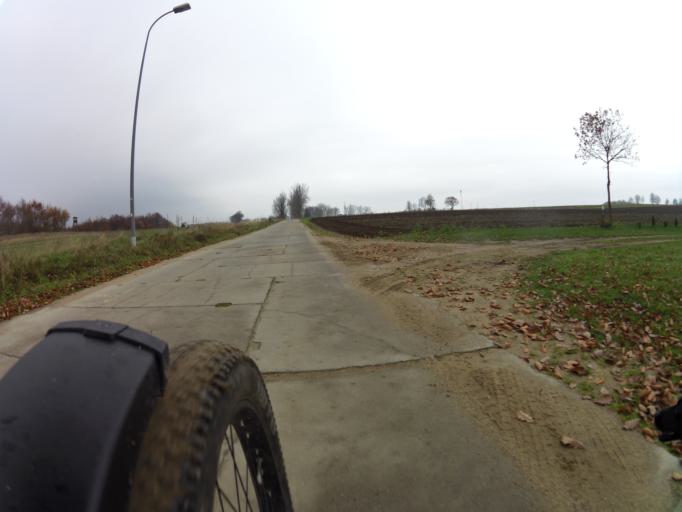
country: PL
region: Pomeranian Voivodeship
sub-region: Powiat pucki
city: Krokowa
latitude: 54.7187
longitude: 18.1384
